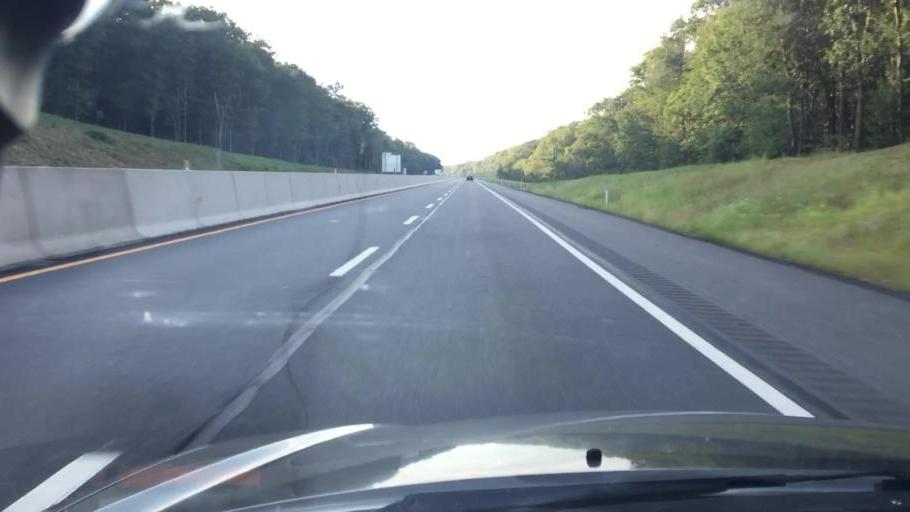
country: US
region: Pennsylvania
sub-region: Carbon County
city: Towamensing Trails
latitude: 41.0155
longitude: -75.6404
